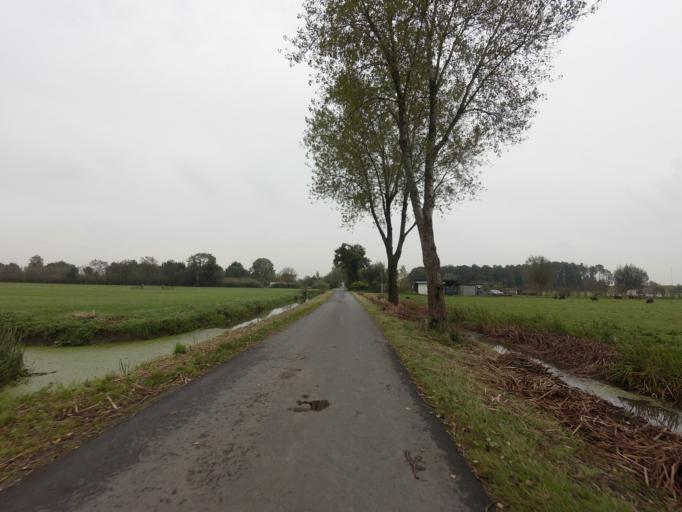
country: NL
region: Utrecht
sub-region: Gemeente Vianen
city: Vianen
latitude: 51.9518
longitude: 5.1342
